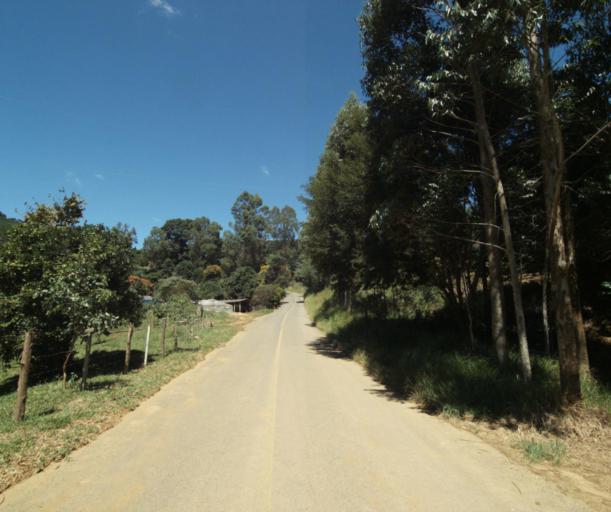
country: BR
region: Minas Gerais
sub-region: Espera Feliz
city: Espera Feliz
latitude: -20.6050
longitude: -41.8334
